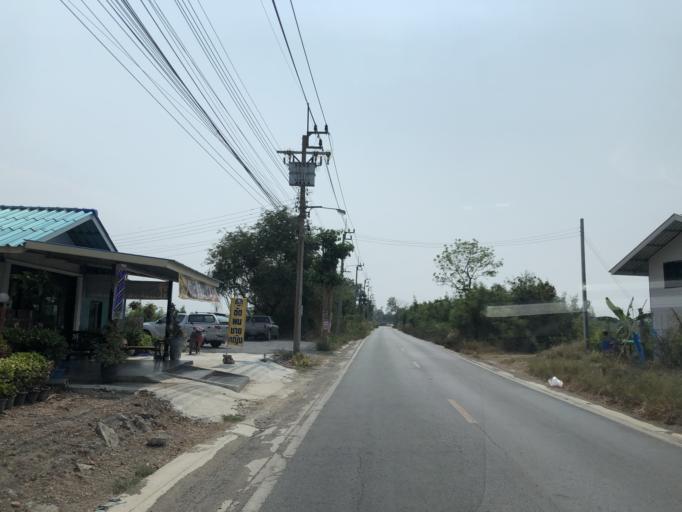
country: TH
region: Samut Prakan
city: Bang Bo
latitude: 13.5437
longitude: 100.8748
